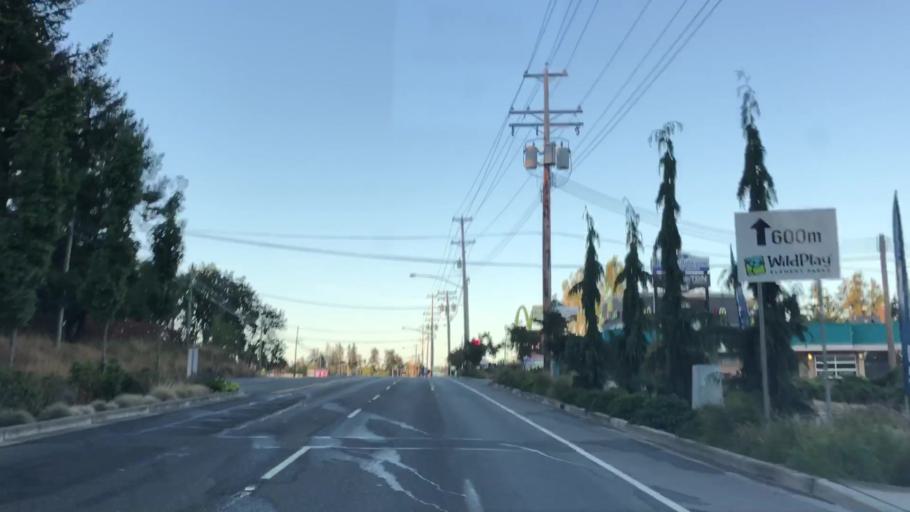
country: CA
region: British Columbia
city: Colwood
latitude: 48.4497
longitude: -123.4648
